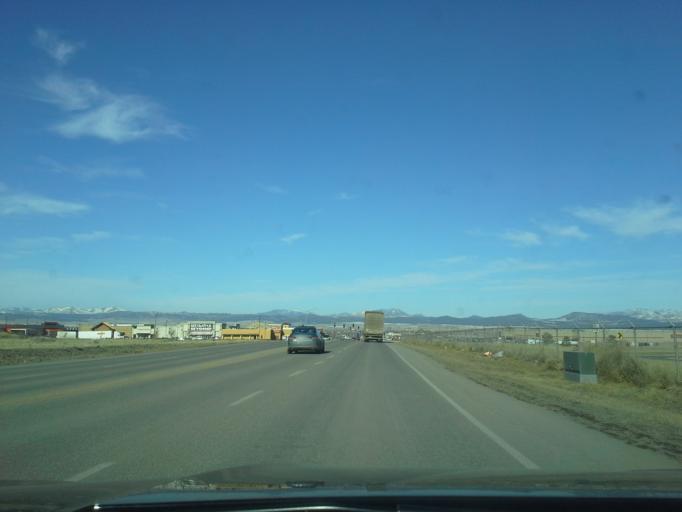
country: US
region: Montana
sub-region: Lewis and Clark County
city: Helena
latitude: 46.6101
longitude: -112.0047
